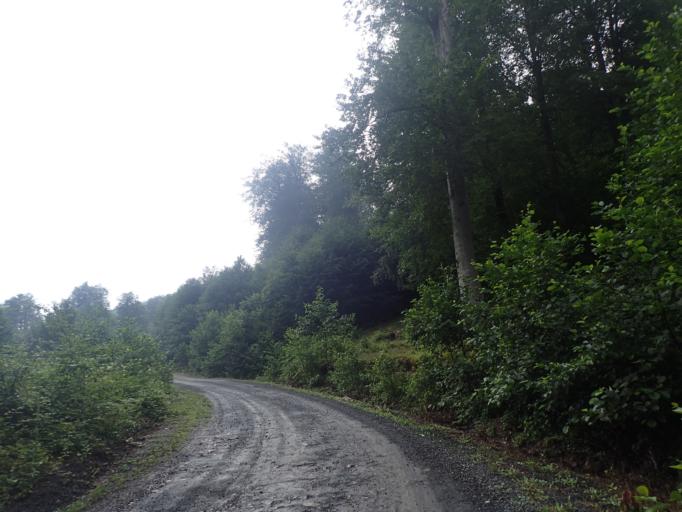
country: TR
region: Ordu
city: Akkus
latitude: 40.8121
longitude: 37.0934
